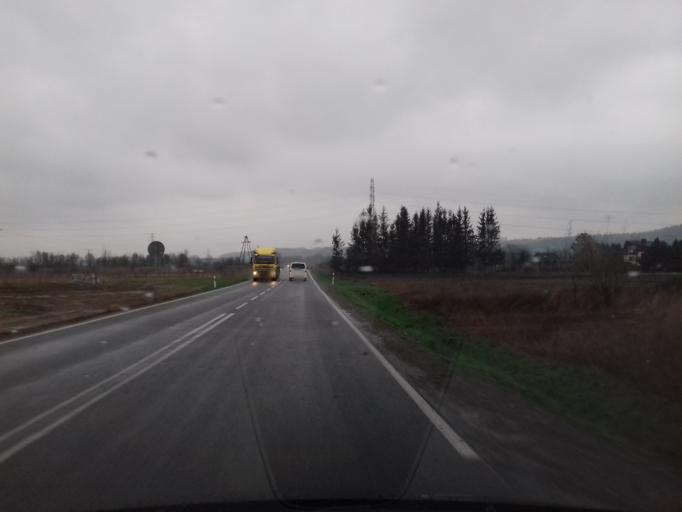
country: PL
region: Lesser Poland Voivodeship
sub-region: Powiat nowosadecki
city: Stary Sacz
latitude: 49.5435
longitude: 20.6485
